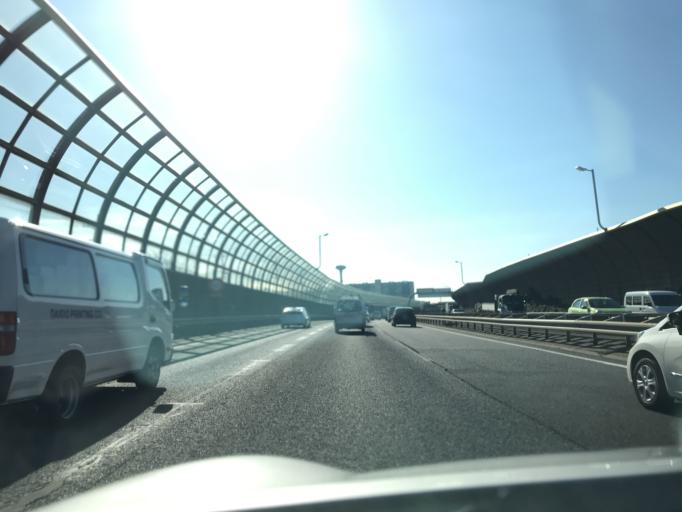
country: JP
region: Chiba
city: Chiba
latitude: 35.6571
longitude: 140.1050
